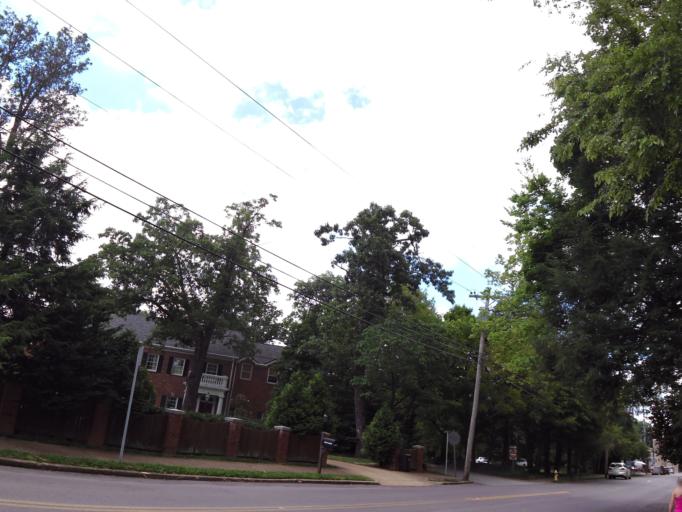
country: US
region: Tennessee
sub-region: Hamilton County
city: Lookout Mountain
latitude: 35.0082
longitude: -85.3434
